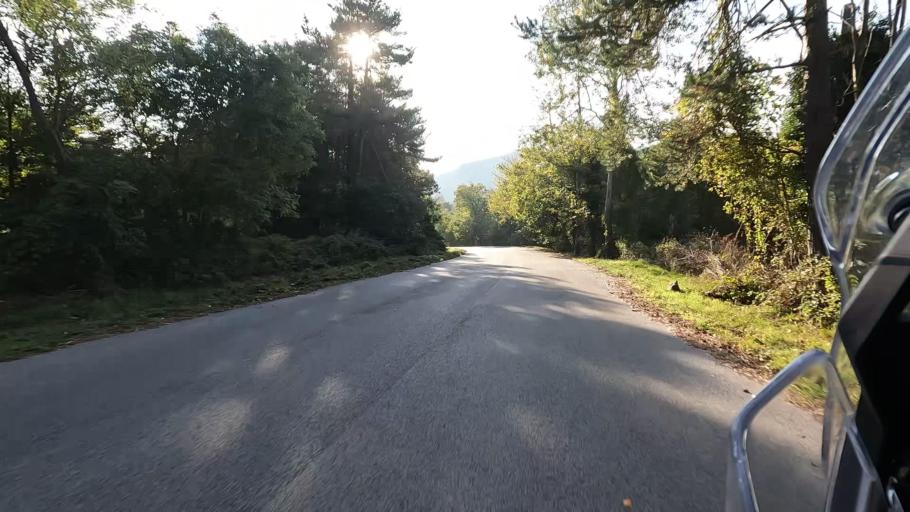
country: IT
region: Liguria
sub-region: Provincia di Savona
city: San Giovanni
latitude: 44.4145
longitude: 8.5225
